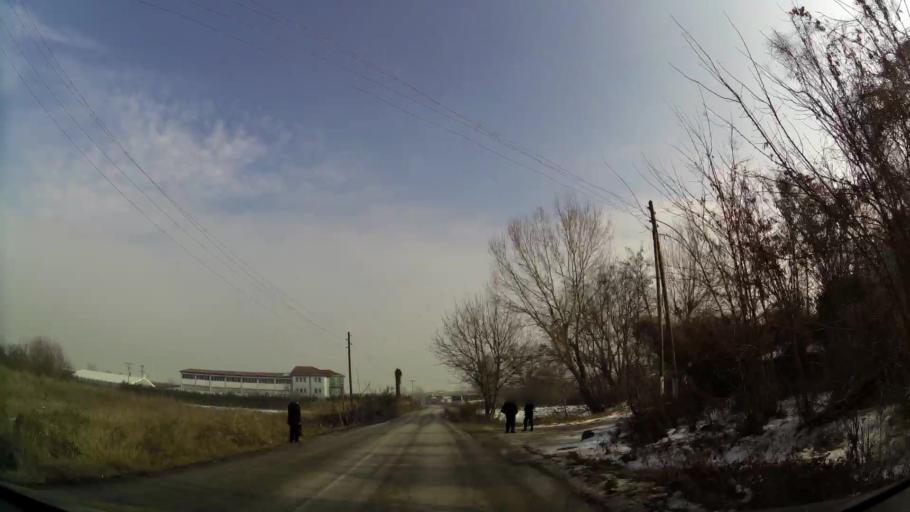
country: MK
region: Ilinden
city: Jurumleri
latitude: 41.9913
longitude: 21.5308
